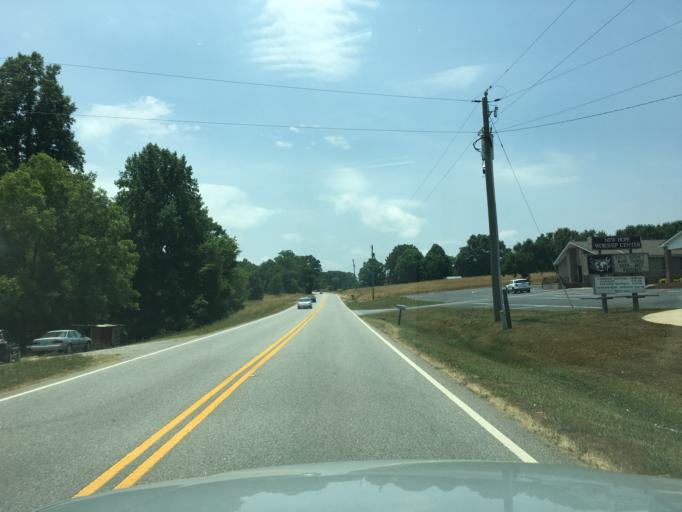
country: US
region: Georgia
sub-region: Hart County
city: Royston
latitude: 34.2363
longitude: -83.1825
